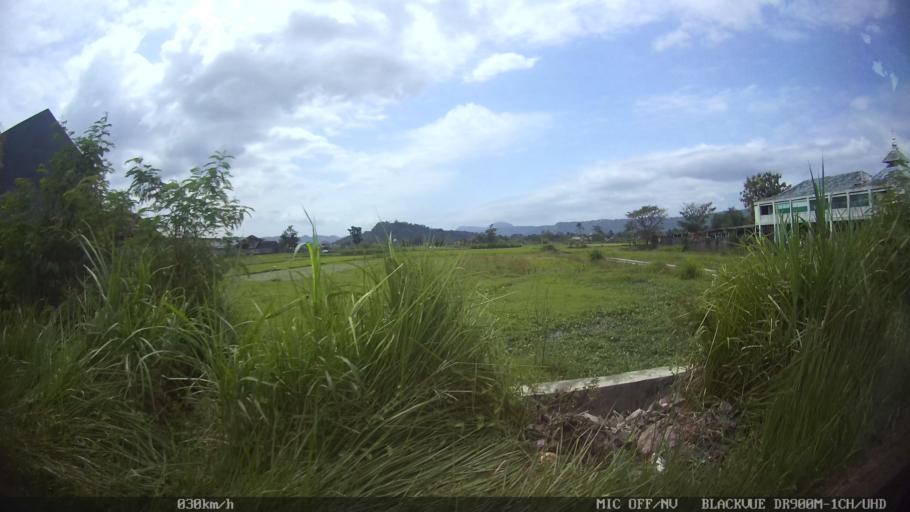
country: ID
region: Daerah Istimewa Yogyakarta
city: Depok
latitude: -7.8232
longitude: 110.4426
